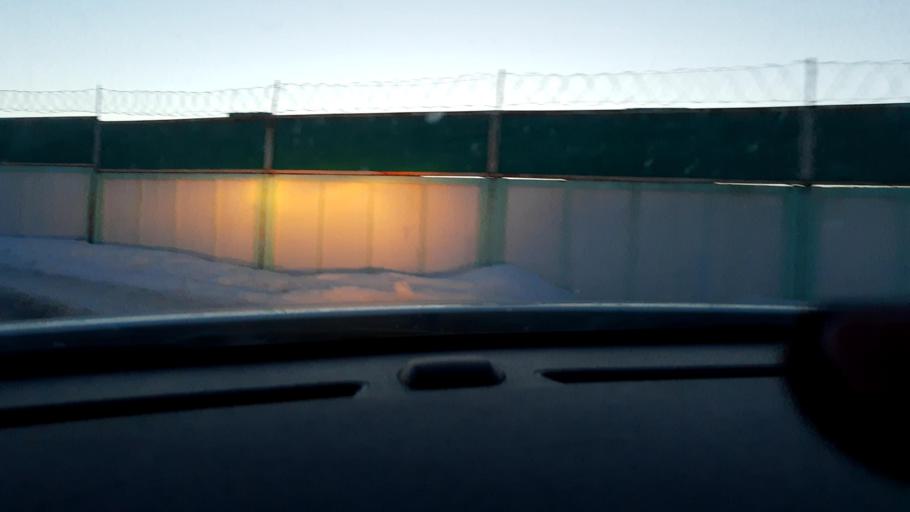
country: RU
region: Bashkortostan
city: Avdon
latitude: 54.3875
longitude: 55.6958
